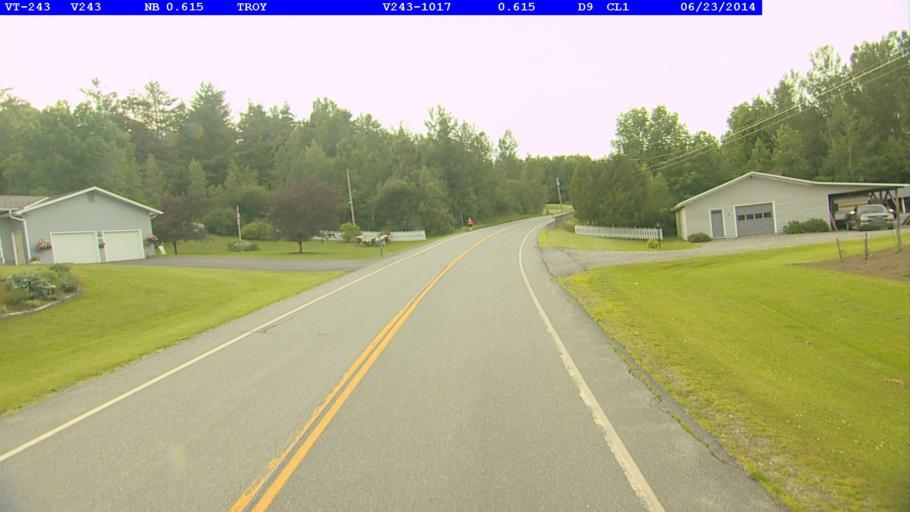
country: US
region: Vermont
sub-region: Orleans County
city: Newport
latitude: 44.9991
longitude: -72.4107
